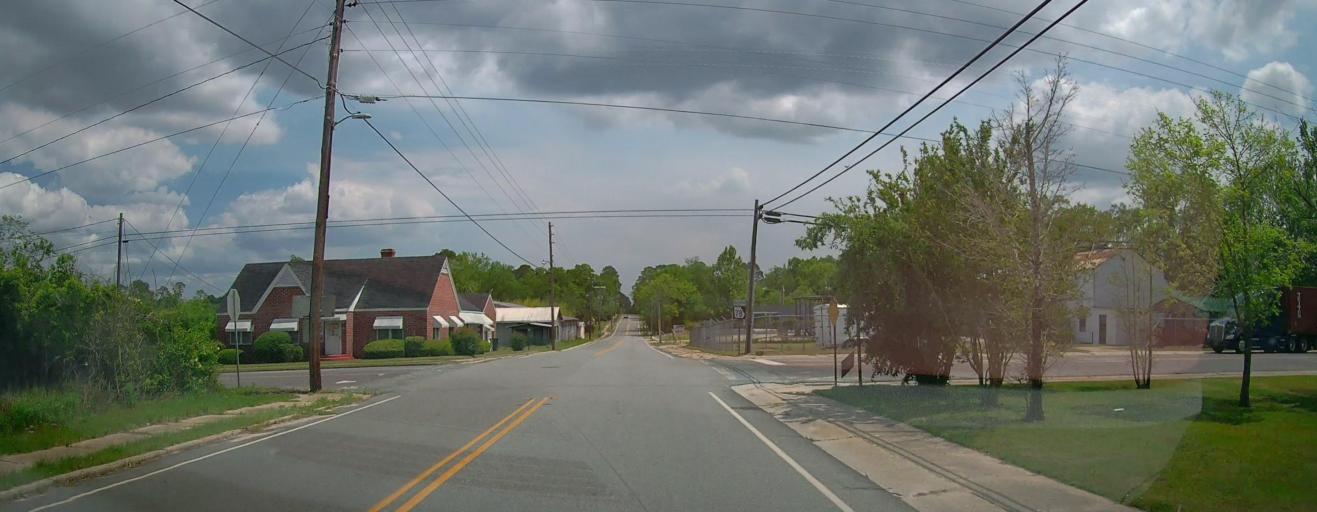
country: US
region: Georgia
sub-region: Treutlen County
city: Soperton
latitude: 32.3784
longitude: -82.5905
